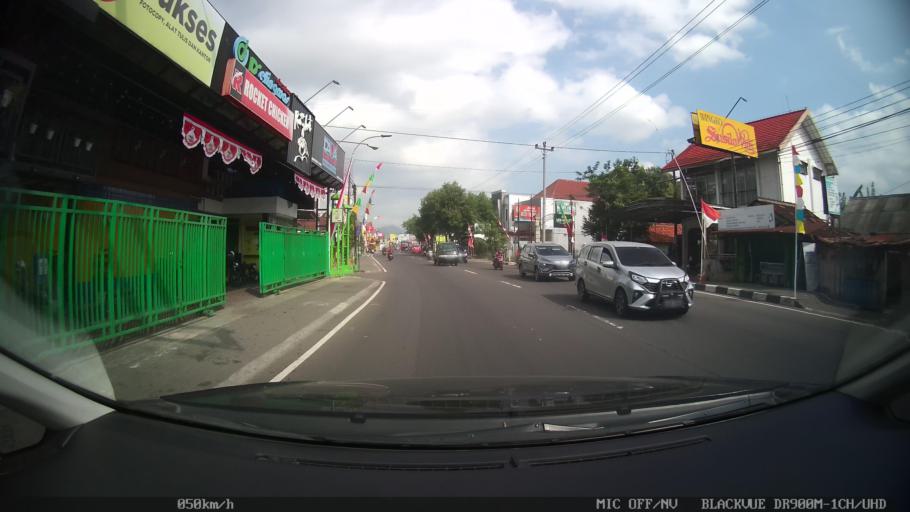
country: ID
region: Daerah Istimewa Yogyakarta
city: Srandakan
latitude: -7.8659
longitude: 110.1598
